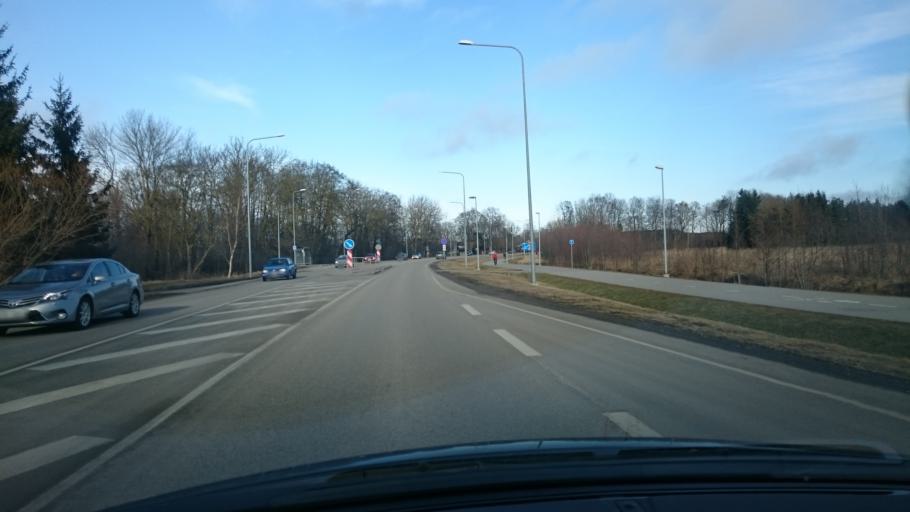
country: EE
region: Harju
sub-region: Harku vald
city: Tabasalu
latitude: 59.4339
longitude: 24.5639
